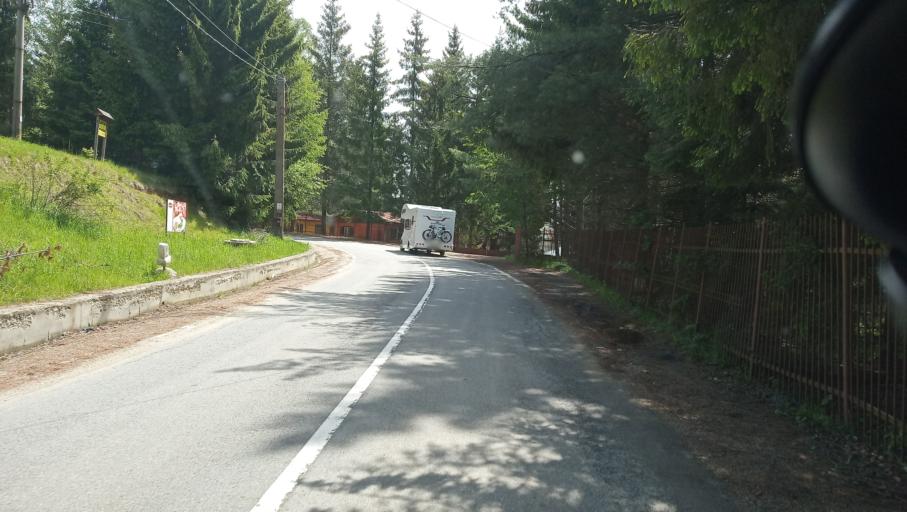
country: RO
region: Caras-Severin
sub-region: Comuna Brebu Nou
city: Brebu Nou
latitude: 45.2148
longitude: 22.1407
